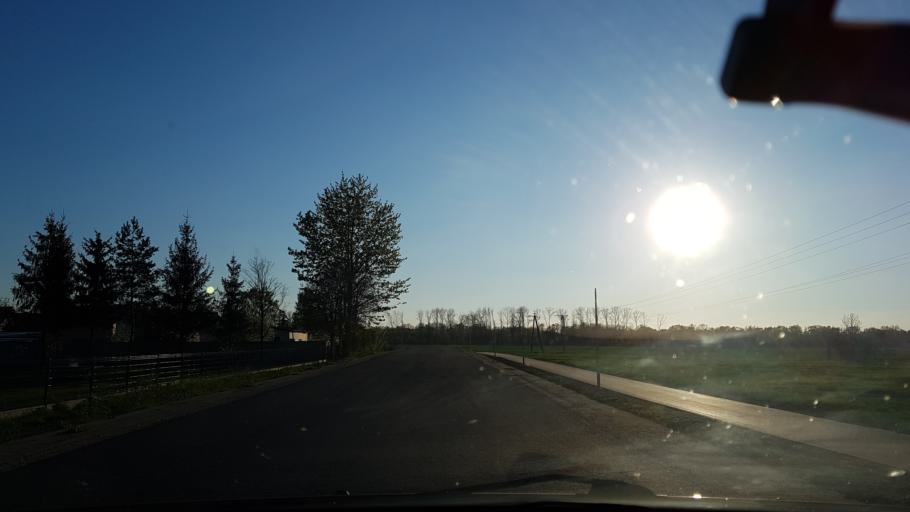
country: PL
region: Opole Voivodeship
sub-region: Powiat nyski
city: Nysa
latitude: 50.4392
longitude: 17.3079
